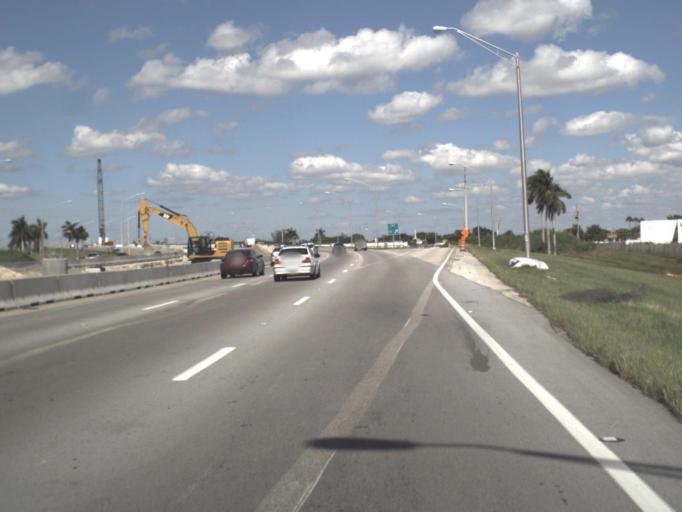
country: US
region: Florida
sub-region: Miami-Dade County
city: South Miami Heights
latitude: 25.5912
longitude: -80.3691
